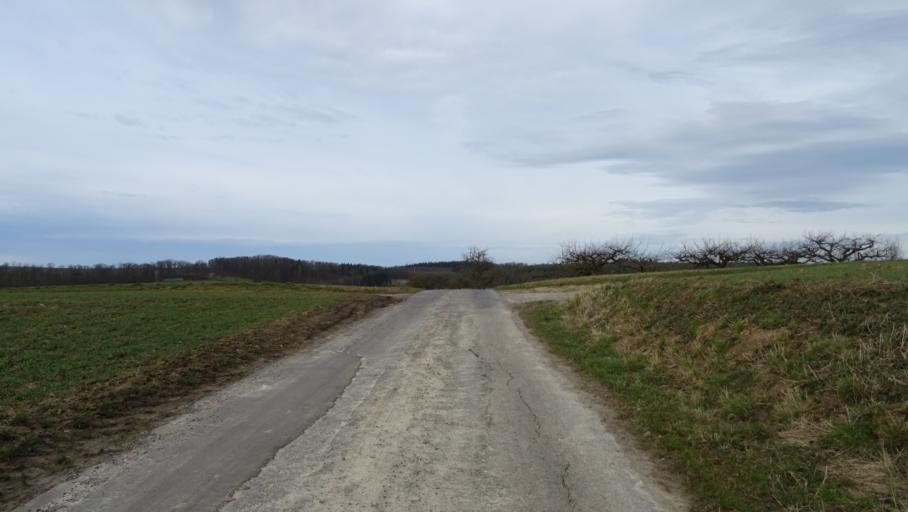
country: DE
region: Baden-Wuerttemberg
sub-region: Karlsruhe Region
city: Seckach
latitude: 49.4271
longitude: 9.2739
